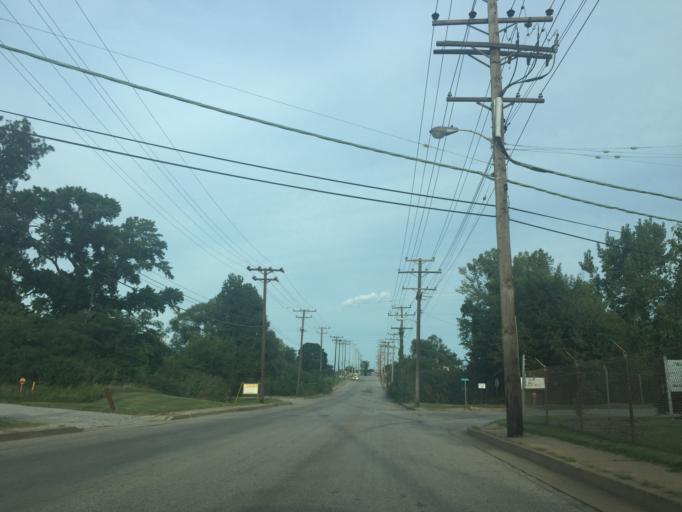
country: US
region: Maryland
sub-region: Anne Arundel County
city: Brooklyn Park
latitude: 39.2322
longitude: -76.5836
